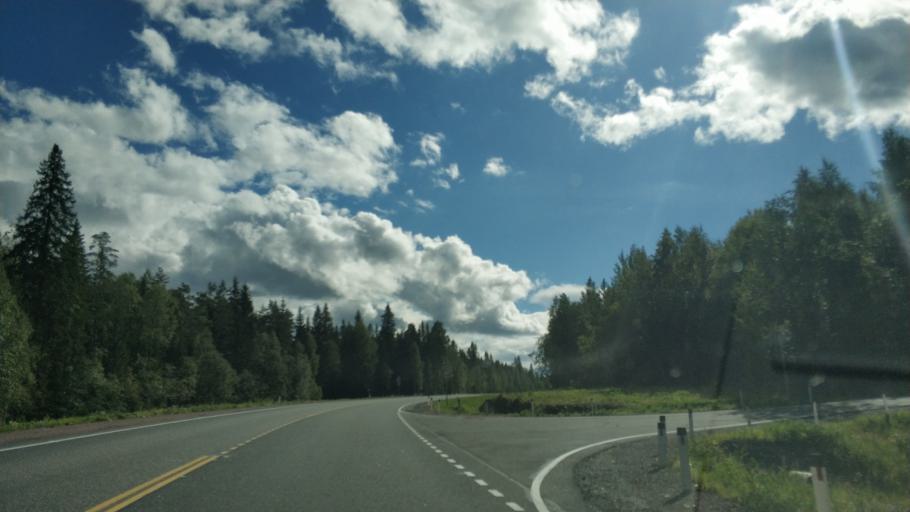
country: RU
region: Republic of Karelia
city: Ruskeala
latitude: 61.8684
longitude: 30.6534
